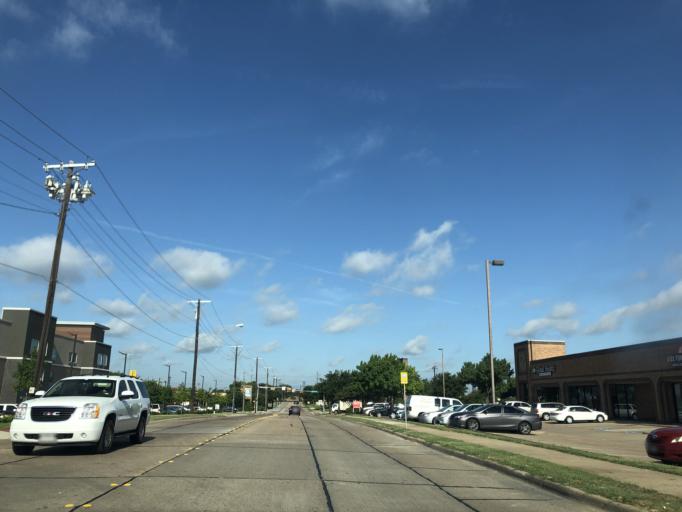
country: US
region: Texas
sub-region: Dallas County
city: Garland
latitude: 32.8595
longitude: -96.6466
